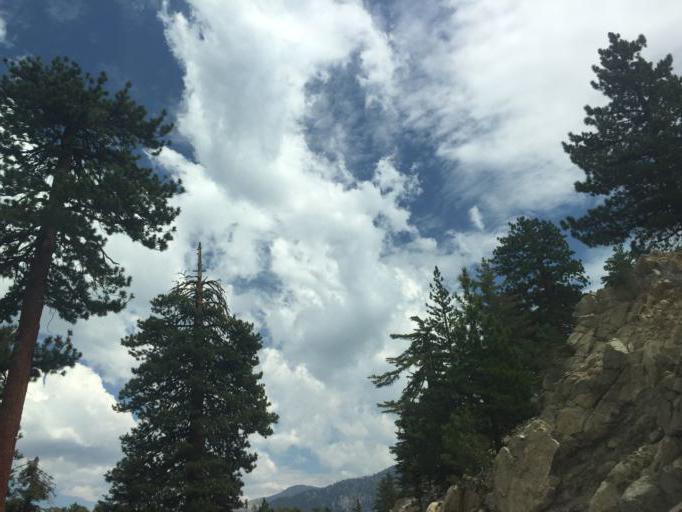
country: US
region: California
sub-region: Los Angeles County
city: Littlerock
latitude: 34.3510
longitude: -117.8845
